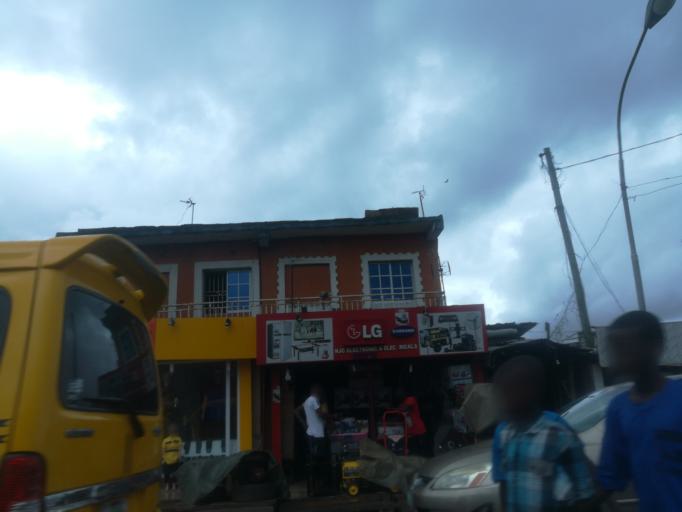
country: NG
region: Lagos
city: Agege
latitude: 6.6253
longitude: 3.3131
